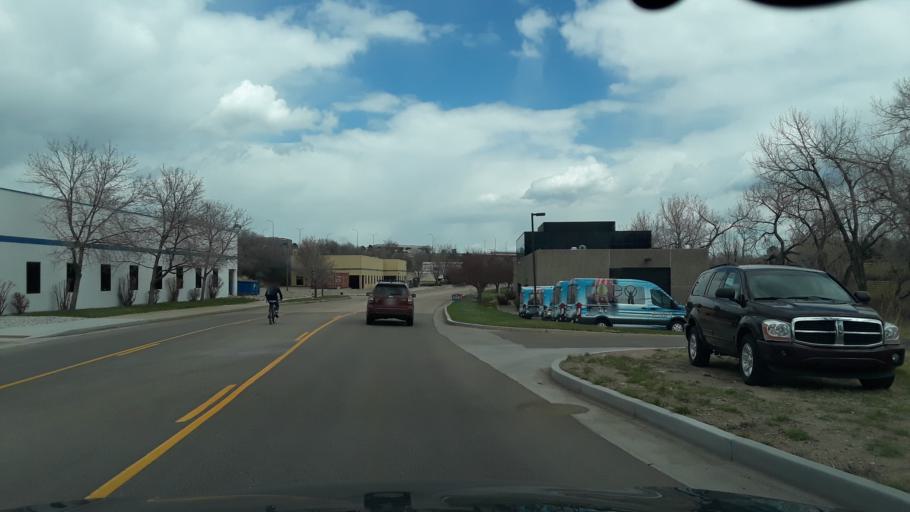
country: US
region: Colorado
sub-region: El Paso County
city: Colorado Springs
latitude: 38.9040
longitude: -104.8242
